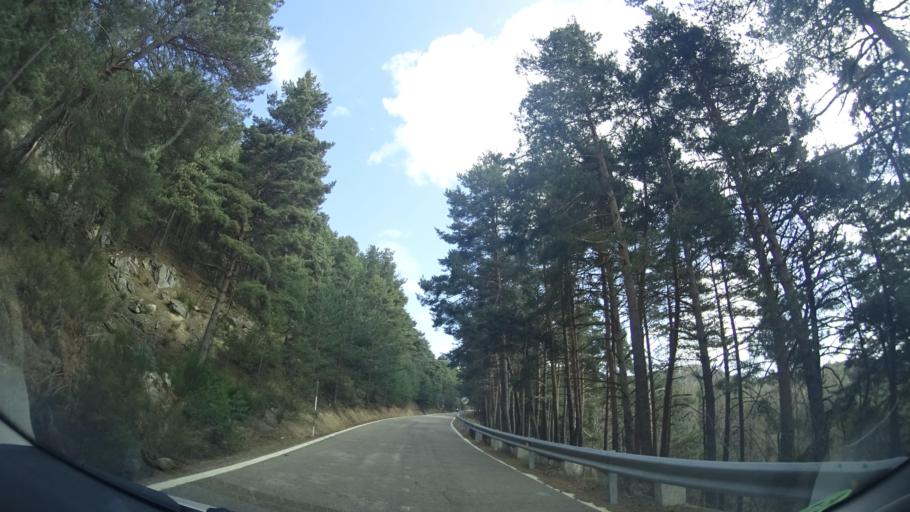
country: ES
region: Madrid
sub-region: Provincia de Madrid
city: Miraflores de la Sierra
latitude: 40.8638
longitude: -3.7642
